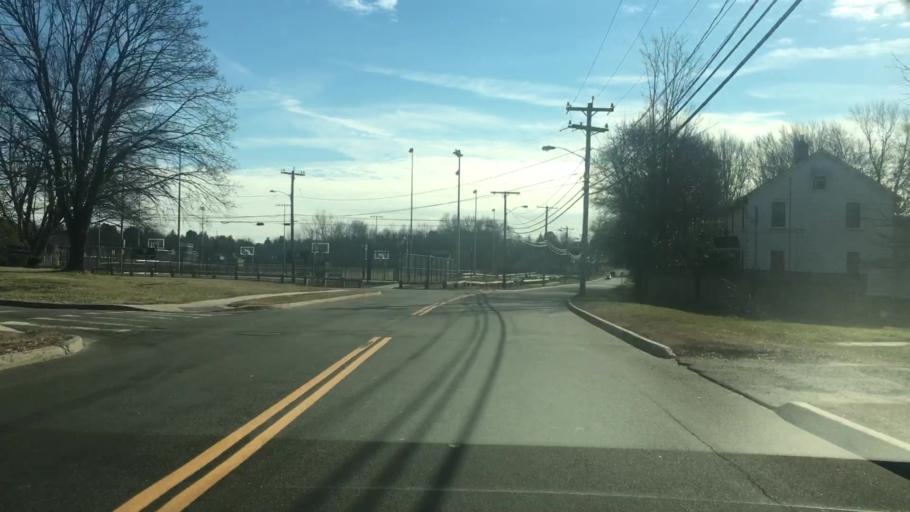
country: US
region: Connecticut
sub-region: Middlesex County
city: Middletown
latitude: 41.5422
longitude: -72.6503
